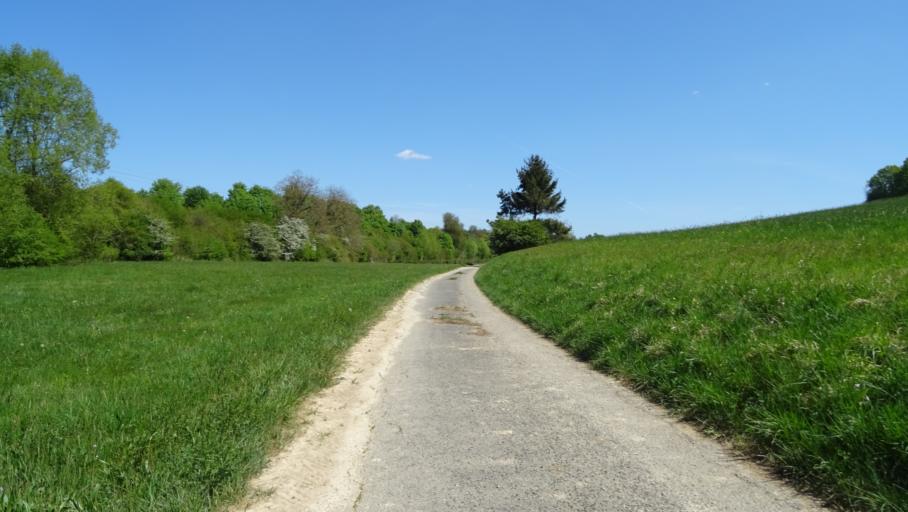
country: DE
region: Baden-Wuerttemberg
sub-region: Karlsruhe Region
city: Limbach
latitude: 49.4138
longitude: 9.2451
